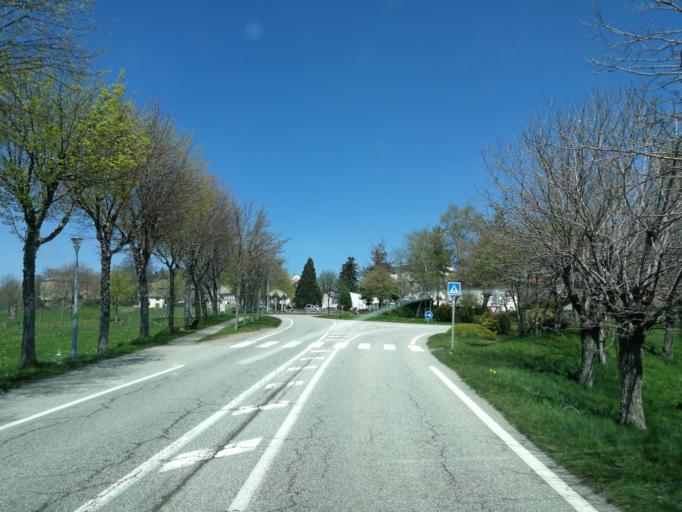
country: FR
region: Rhone-Alpes
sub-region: Departement de l'Ardeche
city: Saint-Agreve
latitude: 45.0055
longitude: 4.4026
